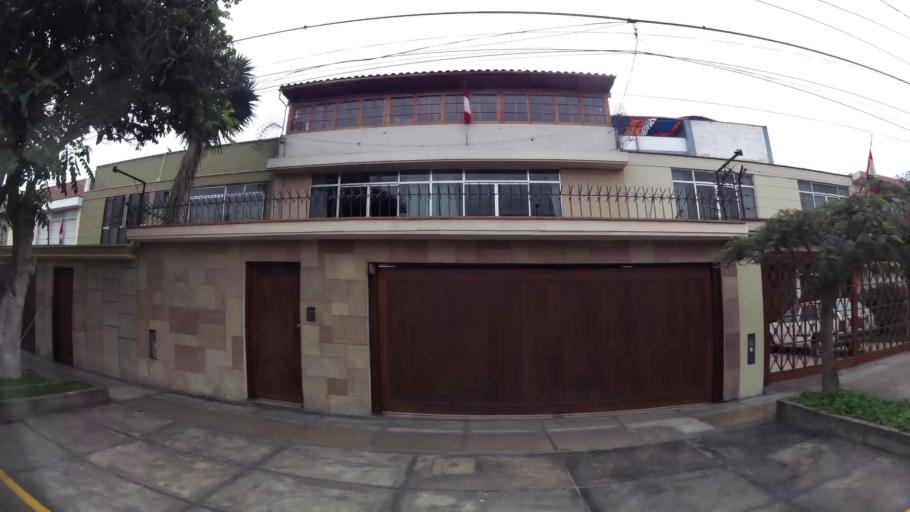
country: PE
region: Lima
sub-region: Lima
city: Surco
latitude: -12.1273
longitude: -76.9978
